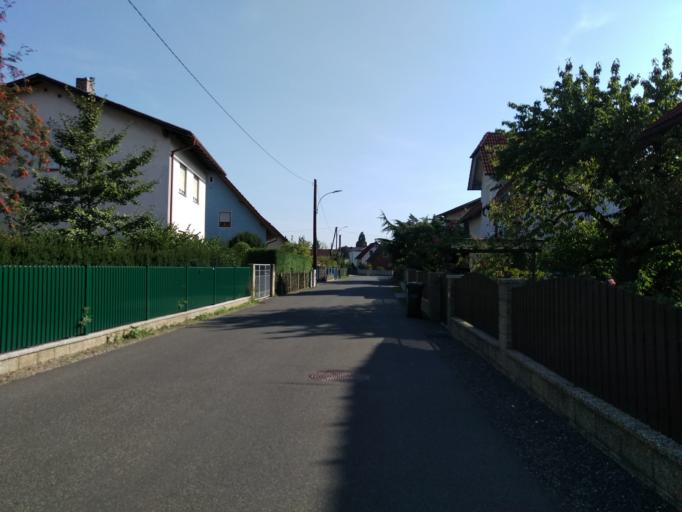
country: AT
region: Styria
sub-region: Politischer Bezirk Graz-Umgebung
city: Feldkirchen bei Graz
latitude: 47.0217
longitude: 15.4288
